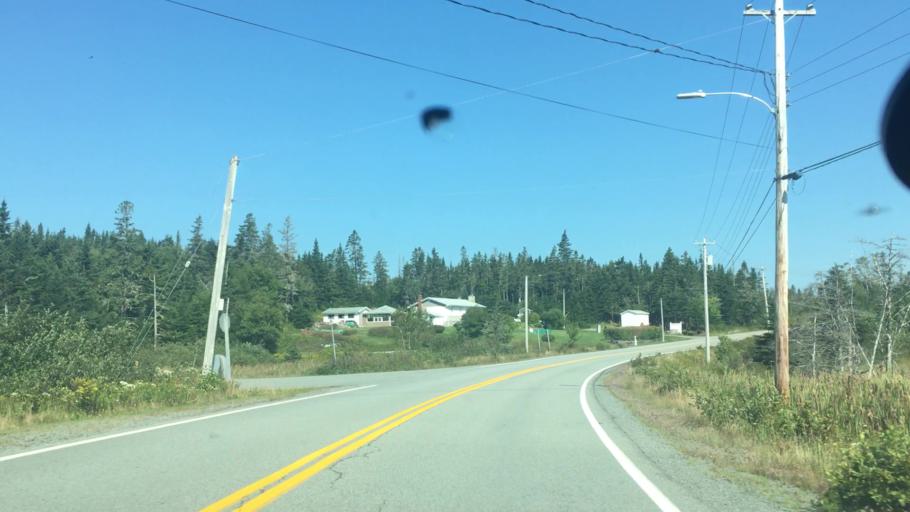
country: CA
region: Nova Scotia
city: New Glasgow
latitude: 44.9269
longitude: -62.2985
